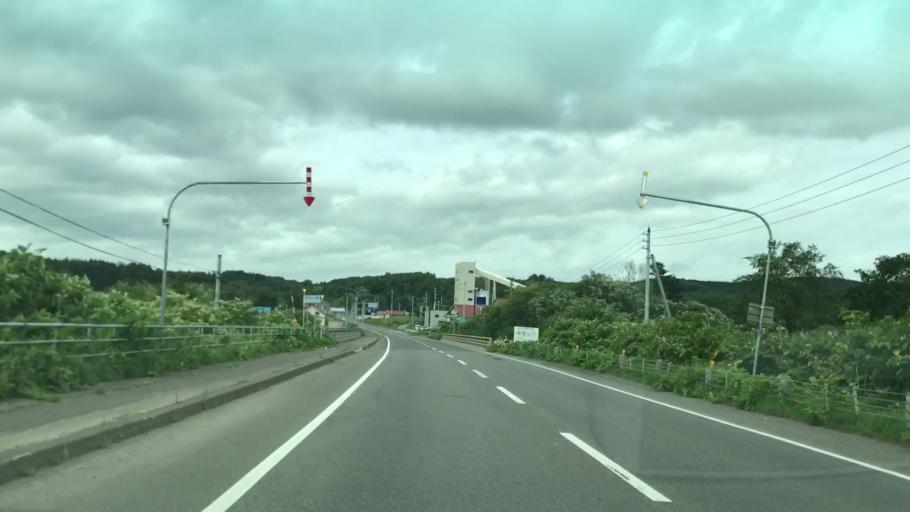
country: JP
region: Hokkaido
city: Niseko Town
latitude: 42.9191
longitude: 140.7443
